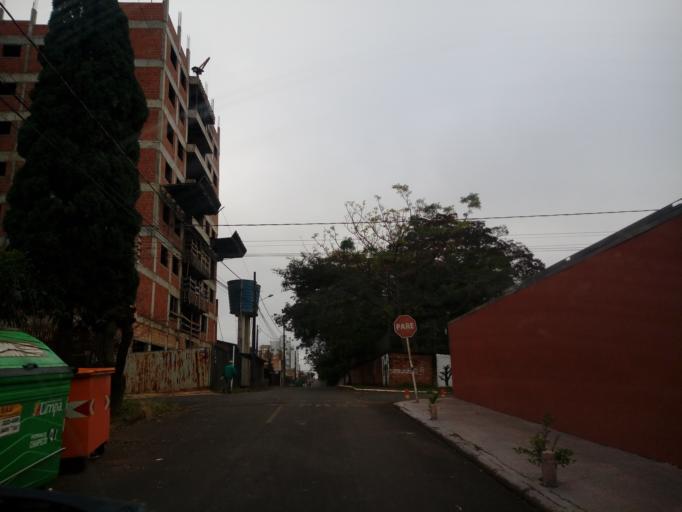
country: BR
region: Santa Catarina
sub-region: Chapeco
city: Chapeco
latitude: -27.0941
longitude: -52.6314
